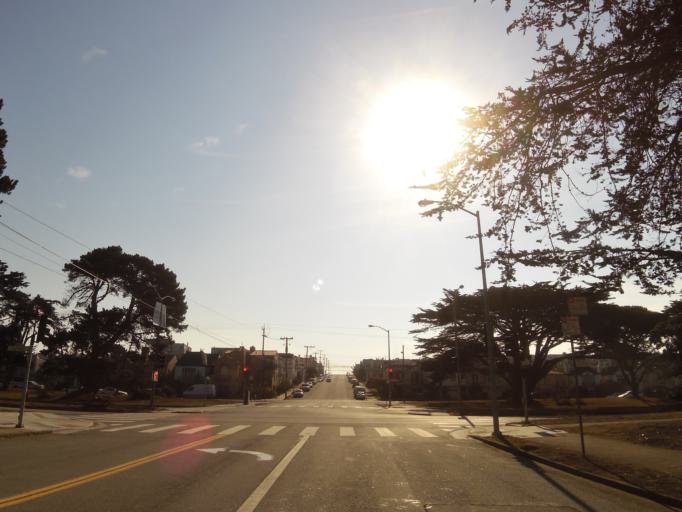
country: US
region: California
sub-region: San Mateo County
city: Daly City
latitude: 37.7571
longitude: -122.4960
